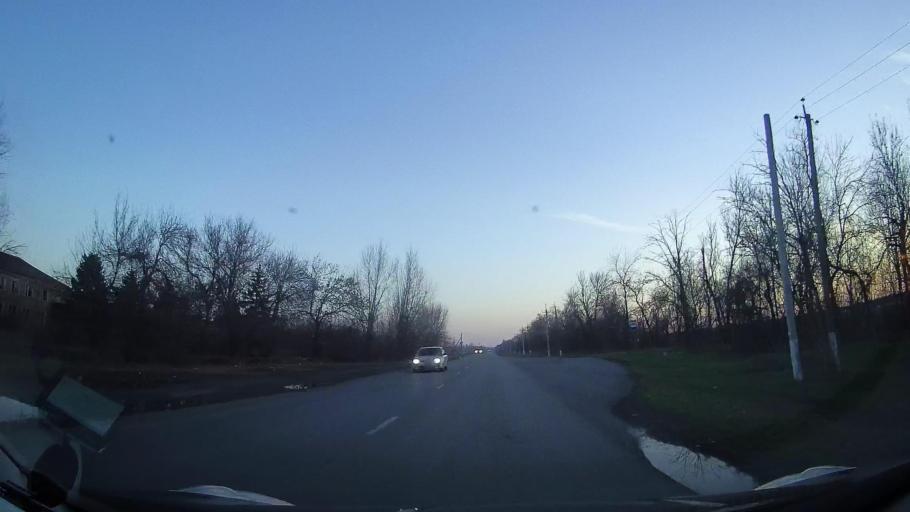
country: RU
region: Rostov
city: Zernograd
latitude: 47.0493
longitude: 40.3915
